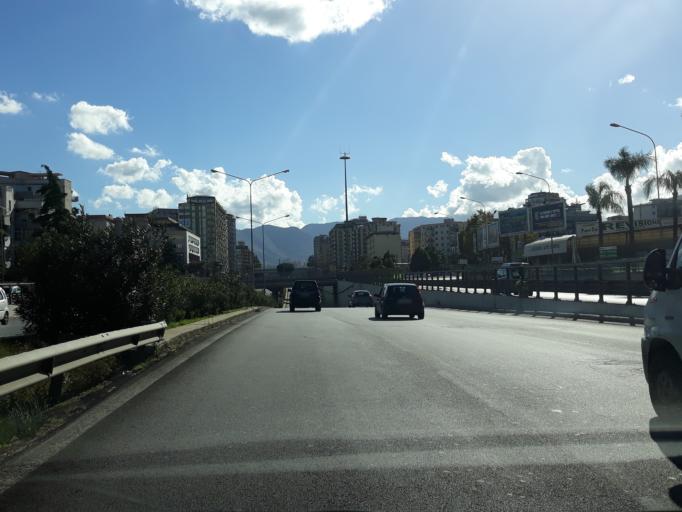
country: IT
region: Sicily
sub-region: Palermo
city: Palermo
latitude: 38.1312
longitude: 13.3300
